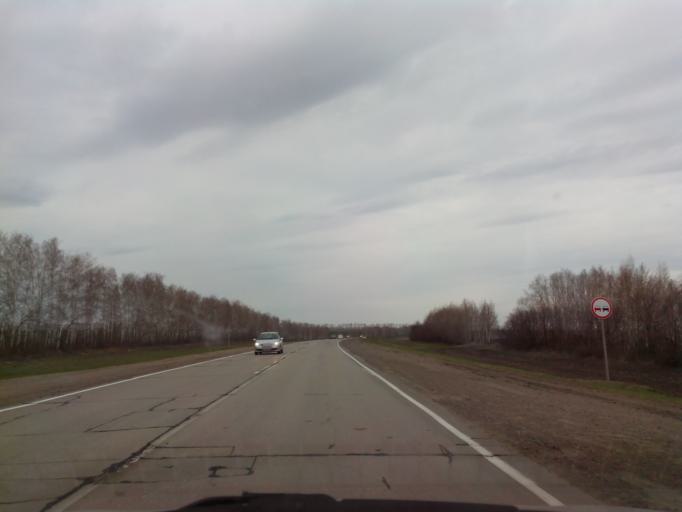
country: RU
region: Tambov
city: Znamenka
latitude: 52.4138
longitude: 41.3792
